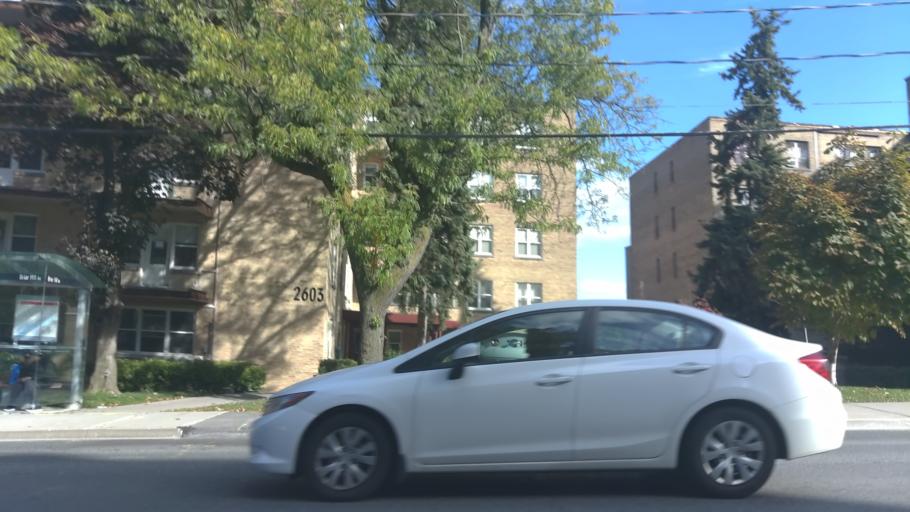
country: CA
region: Ontario
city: Toronto
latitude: 43.7077
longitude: -79.4270
